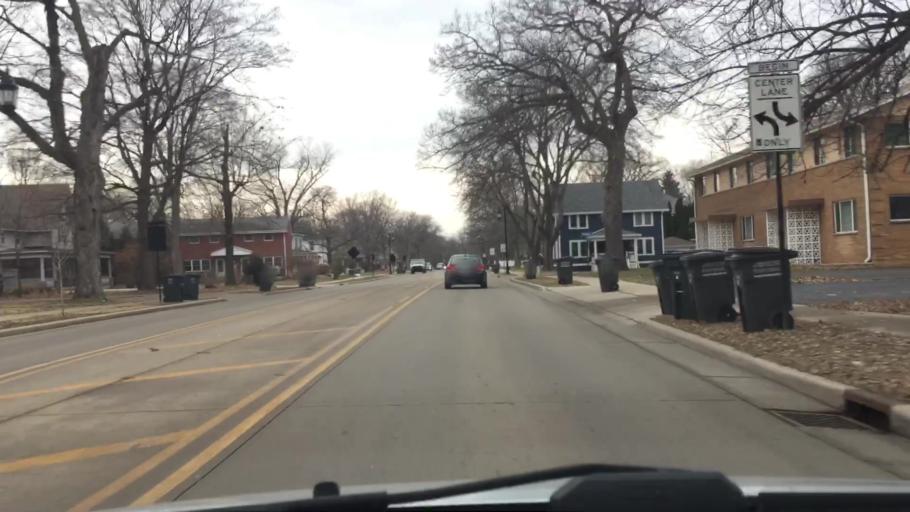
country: US
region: Wisconsin
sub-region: Waukesha County
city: Oconomowoc
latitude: 43.1129
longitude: -88.5060
